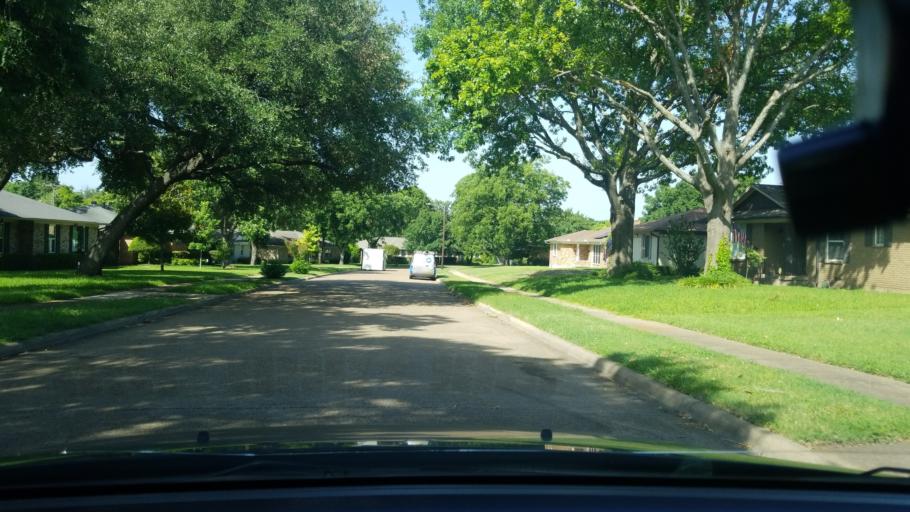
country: US
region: Texas
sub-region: Dallas County
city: Mesquite
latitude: 32.7995
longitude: -96.6937
